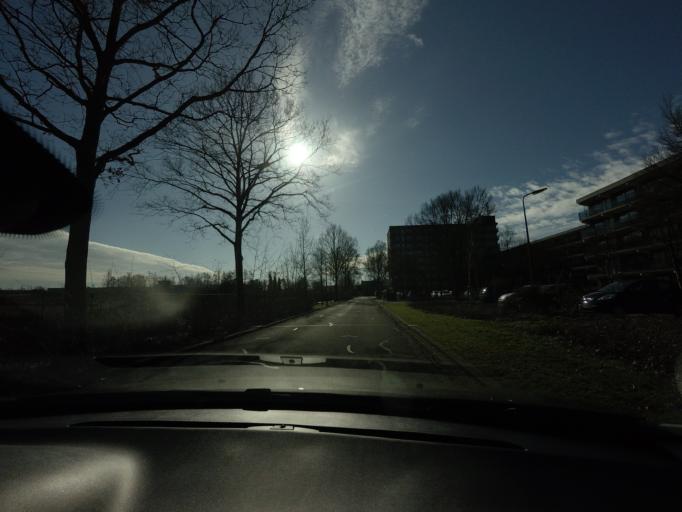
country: NL
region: Utrecht
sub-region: Gemeente Woerden
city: Woerden
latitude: 52.0931
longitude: 4.9070
